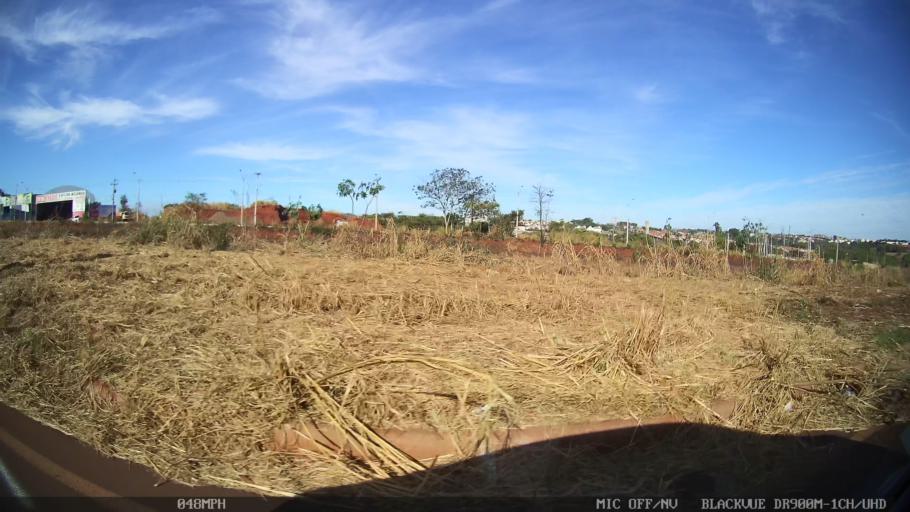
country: BR
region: Sao Paulo
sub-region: Sao Jose Do Rio Preto
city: Sao Jose do Rio Preto
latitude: -20.7711
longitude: -49.3493
